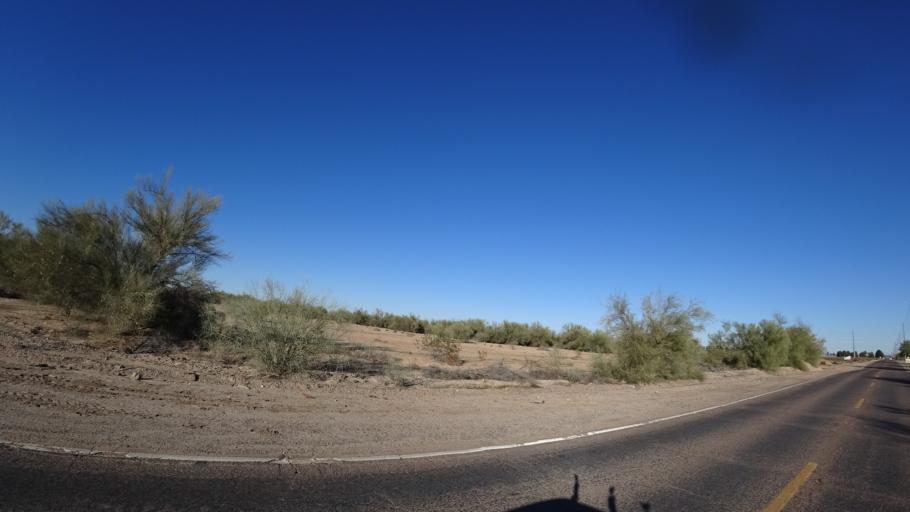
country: US
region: Arizona
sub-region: Maricopa County
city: Citrus Park
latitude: 33.4647
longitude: -112.4700
